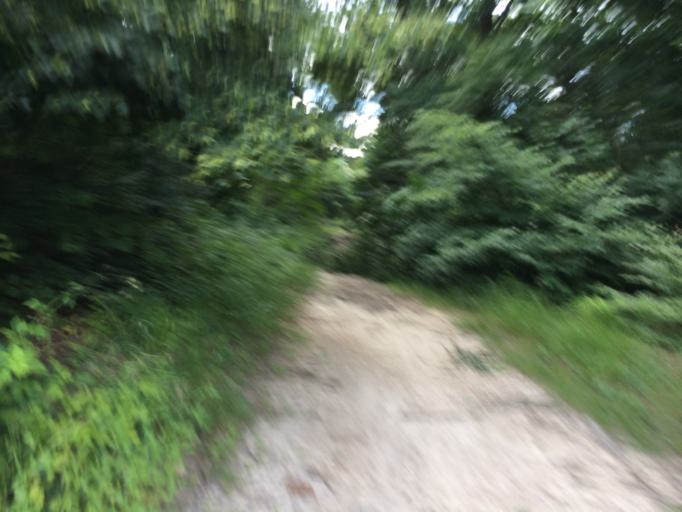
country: FR
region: Ile-de-France
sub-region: Departement de l'Essonne
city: Soisy-sur-Seine
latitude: 48.6643
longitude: 2.4341
